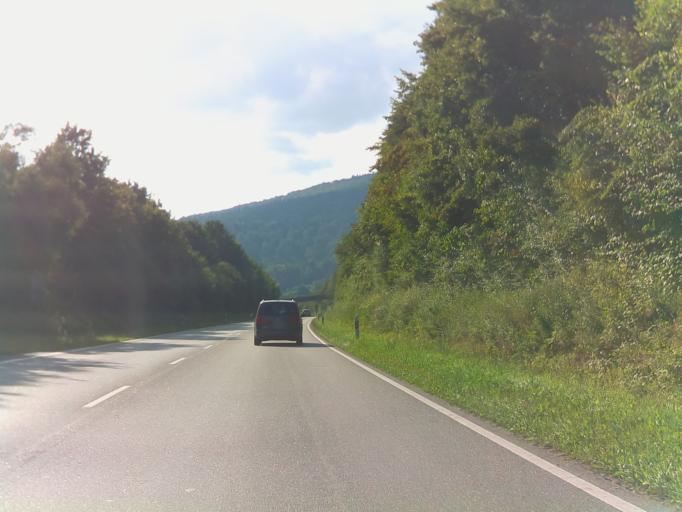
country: DE
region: Bavaria
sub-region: Regierungsbezirk Unterfranken
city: Rieneck
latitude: 50.0642
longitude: 9.6707
